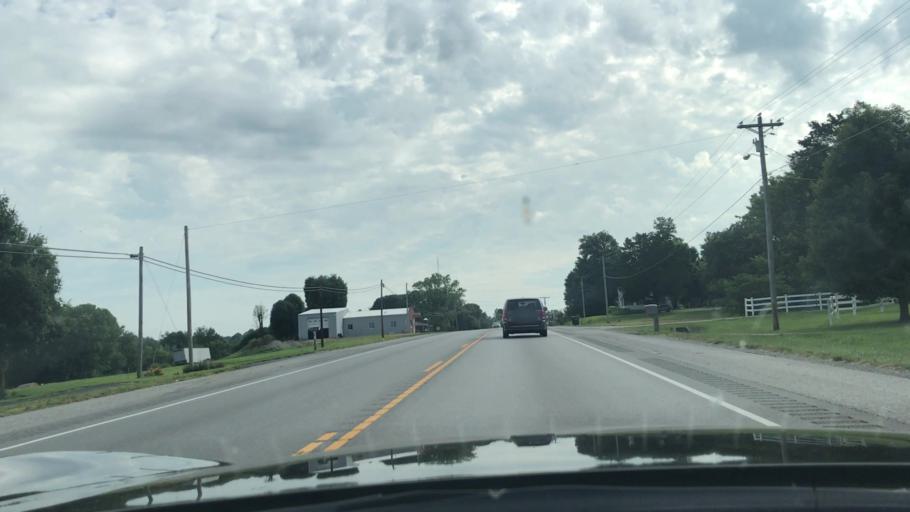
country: US
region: Kentucky
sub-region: Taylor County
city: Campbellsville
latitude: 37.3294
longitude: -85.3859
